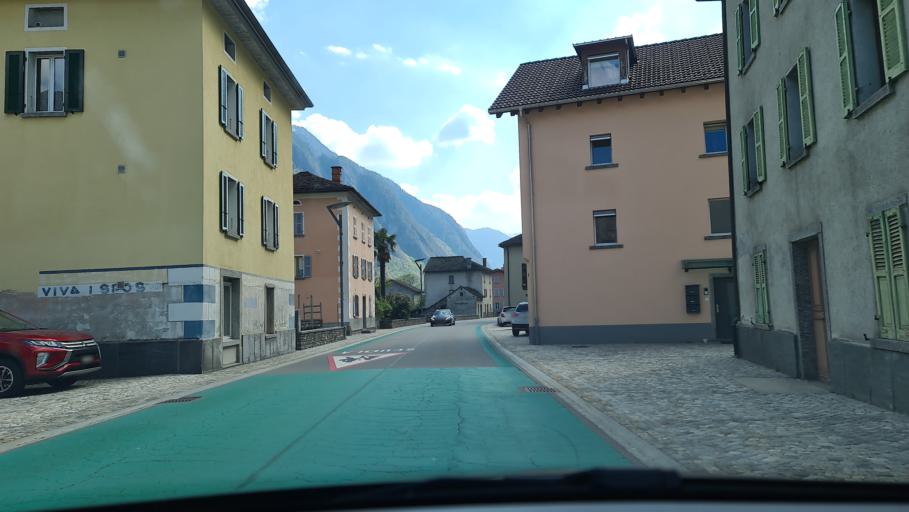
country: CH
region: Grisons
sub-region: Moesa District
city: Santa Maria in Calanca
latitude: 46.3130
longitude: 9.1960
